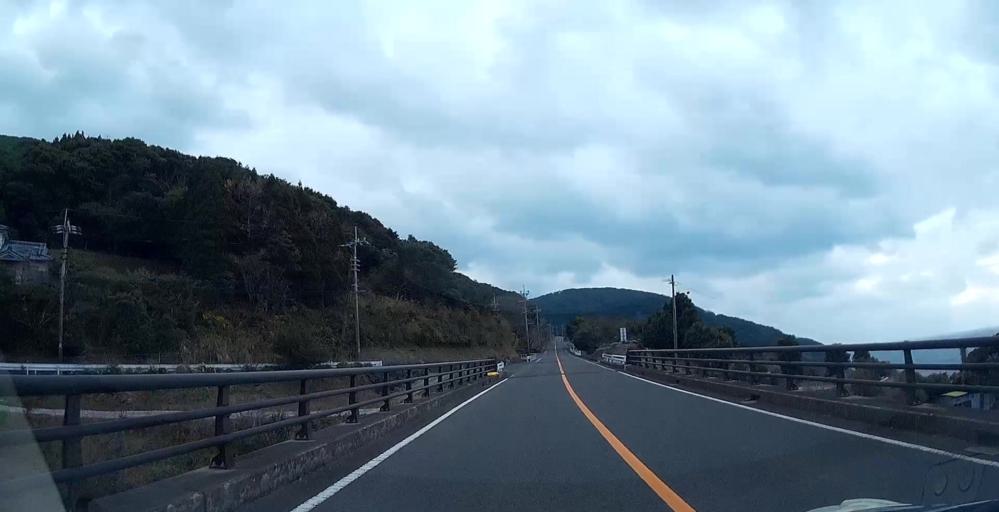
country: JP
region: Kagoshima
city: Akune
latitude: 32.1040
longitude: 130.1509
